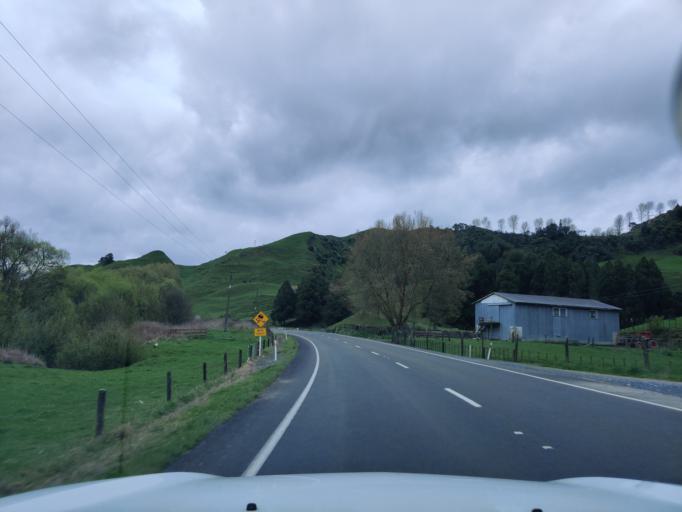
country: NZ
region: Waikato
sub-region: Otorohanga District
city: Otorohanga
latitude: -38.4872
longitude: 175.1860
